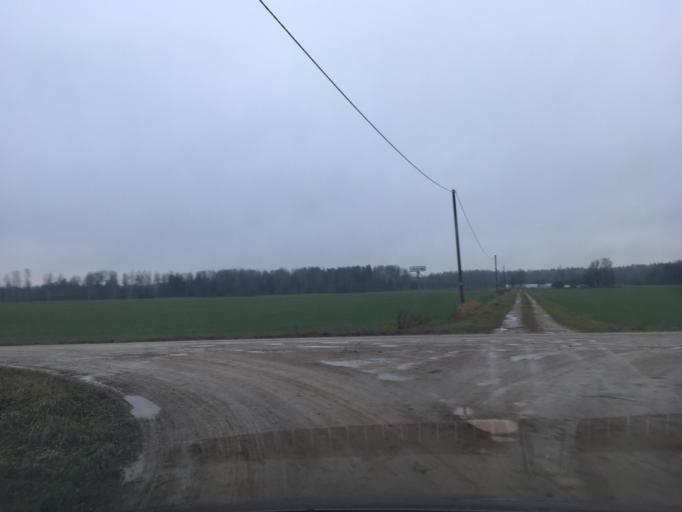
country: EE
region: Tartu
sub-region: Alatskivi vald
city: Kallaste
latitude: 58.3950
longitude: 27.0265
